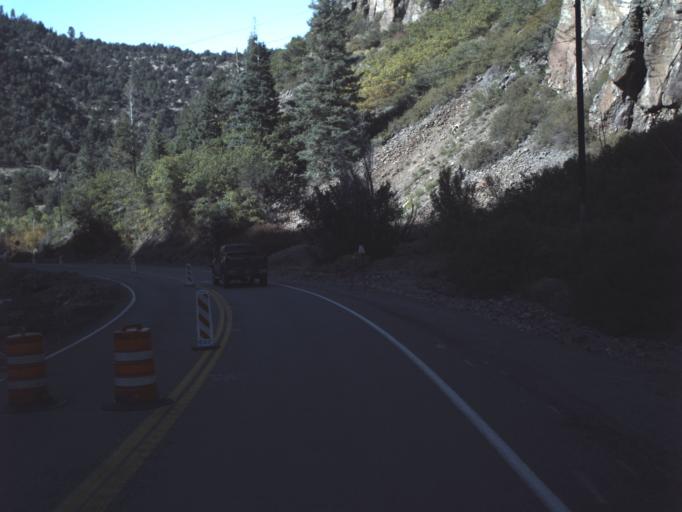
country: US
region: Utah
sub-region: Iron County
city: Parowan
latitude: 37.7601
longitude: -112.8489
